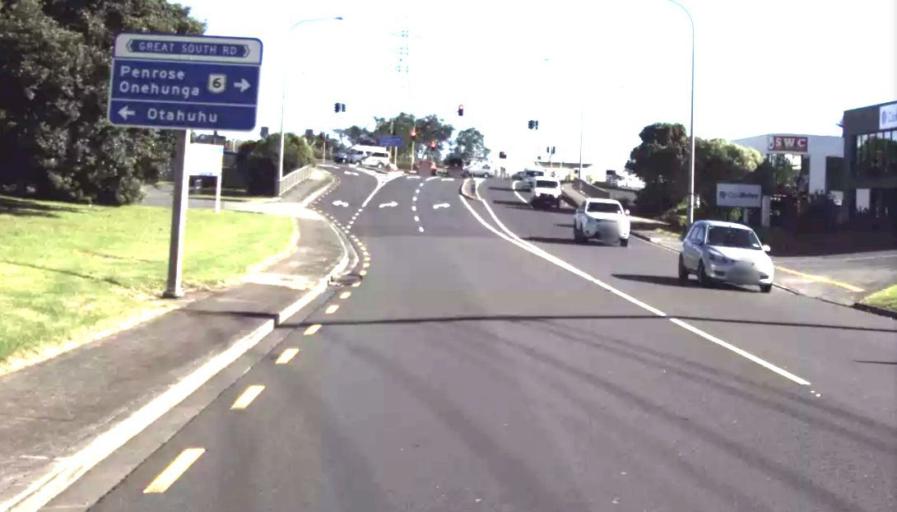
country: NZ
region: Auckland
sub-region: Auckland
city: Tamaki
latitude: -36.9247
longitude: 174.8338
